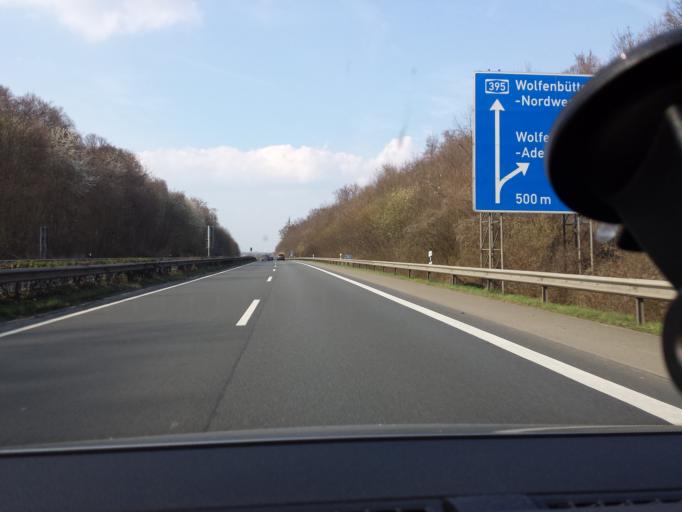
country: DE
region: Lower Saxony
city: Wolfenbuettel
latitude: 52.1465
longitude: 10.4933
